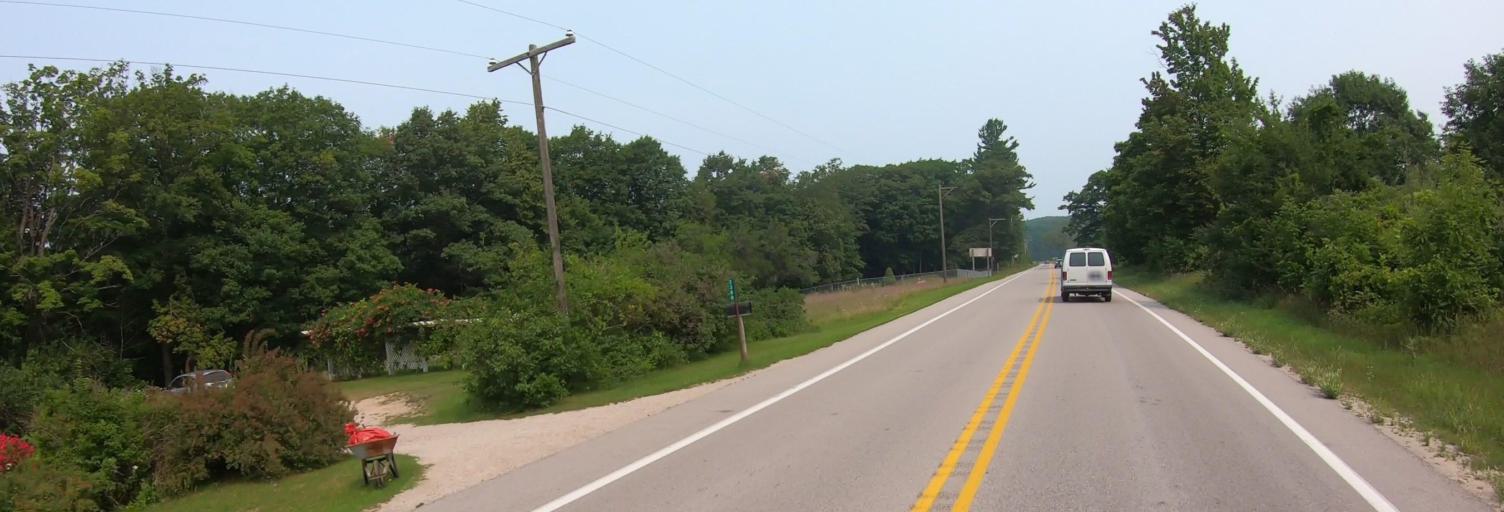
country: US
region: Michigan
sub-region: Leelanau County
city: Leland
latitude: 44.9453
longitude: -85.8015
